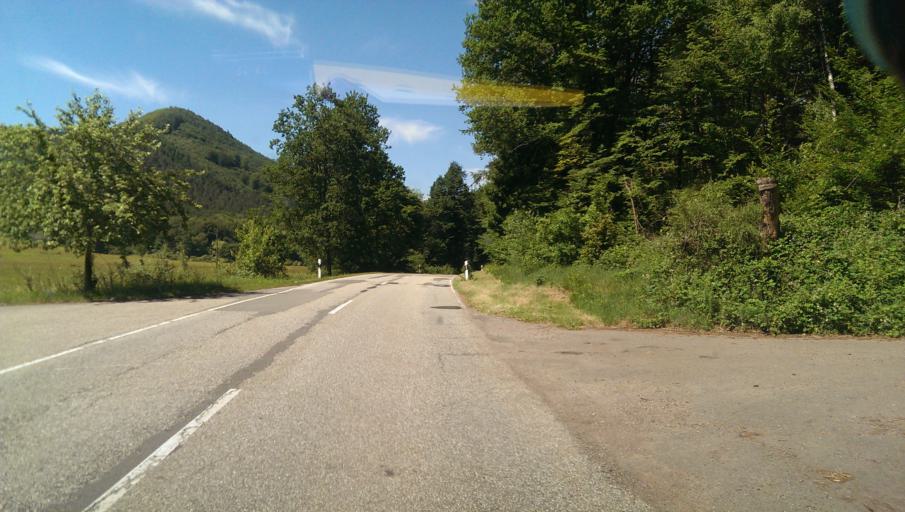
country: DE
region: Rheinland-Pfalz
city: Rumbach
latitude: 49.0845
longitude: 7.7831
